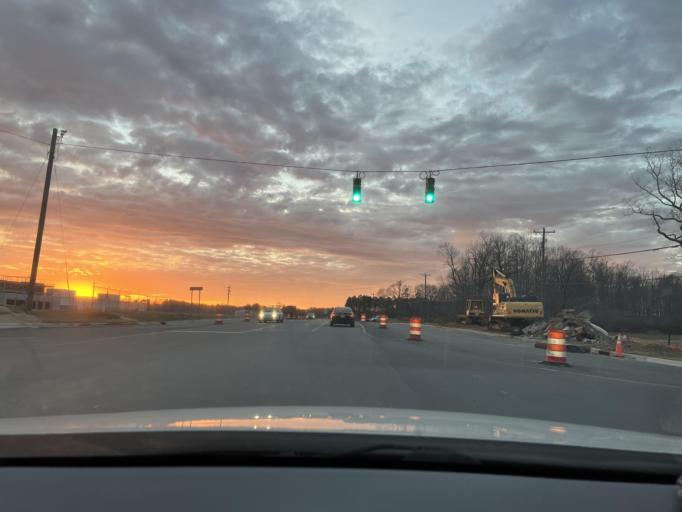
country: US
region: North Carolina
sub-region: Guilford County
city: McLeansville
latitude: 36.0852
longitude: -79.6598
